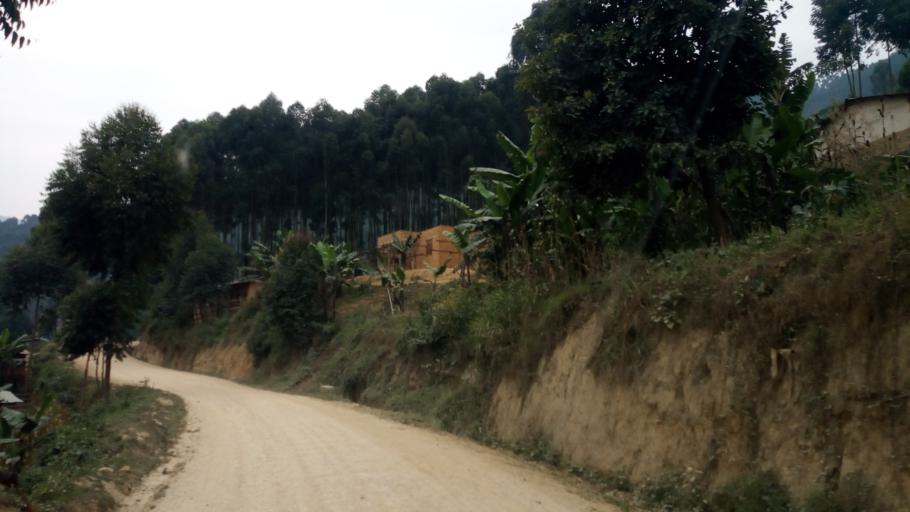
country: UG
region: Western Region
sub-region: Kanungu District
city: Kanungu
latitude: -1.1070
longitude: 29.8640
